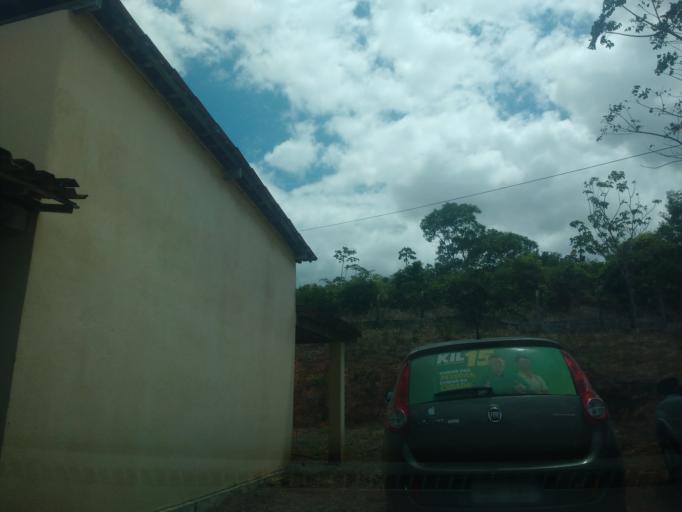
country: BR
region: Alagoas
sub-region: Santana Do Mundau
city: Santana do Mundau
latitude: -9.1586
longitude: -36.1603
